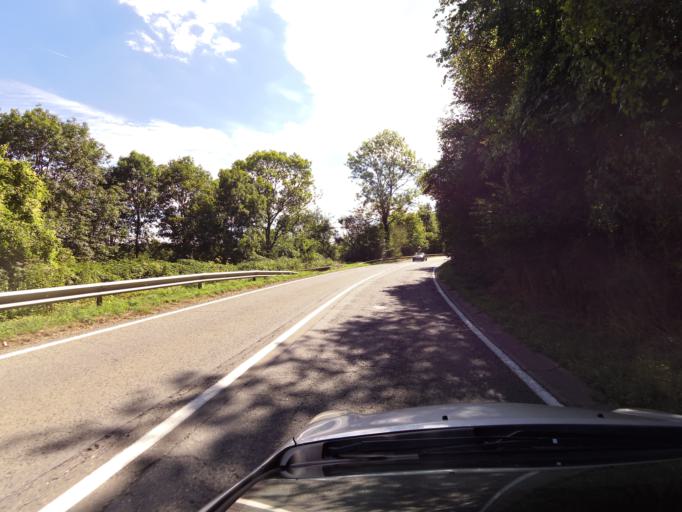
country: BE
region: Wallonia
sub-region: Province du Luxembourg
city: Hotton
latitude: 50.2641
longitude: 5.4605
